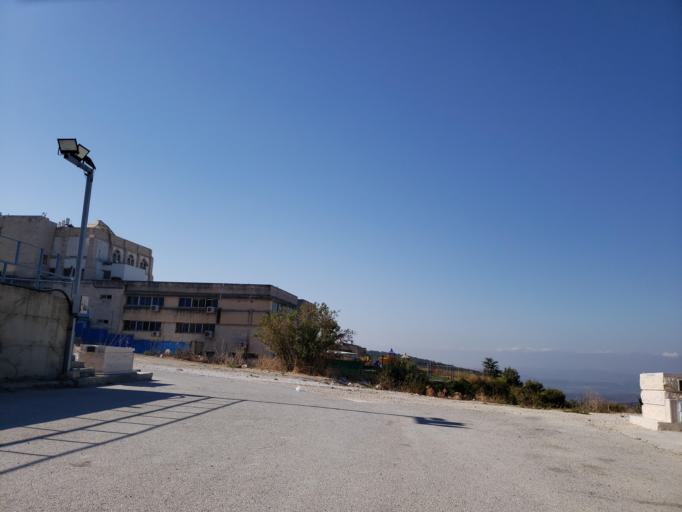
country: IL
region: Northern District
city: Safed
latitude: 32.9671
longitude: 35.4862
